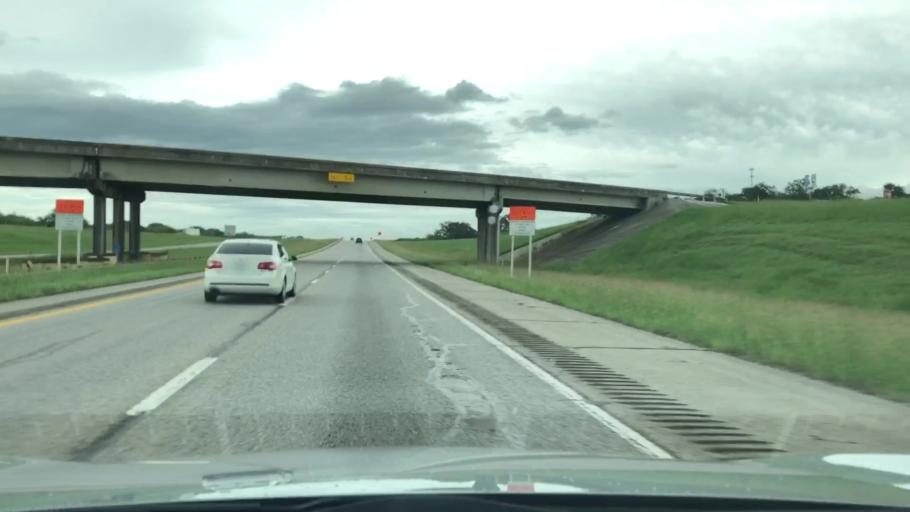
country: US
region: Texas
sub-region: Caldwell County
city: Luling
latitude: 29.6198
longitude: -97.7878
